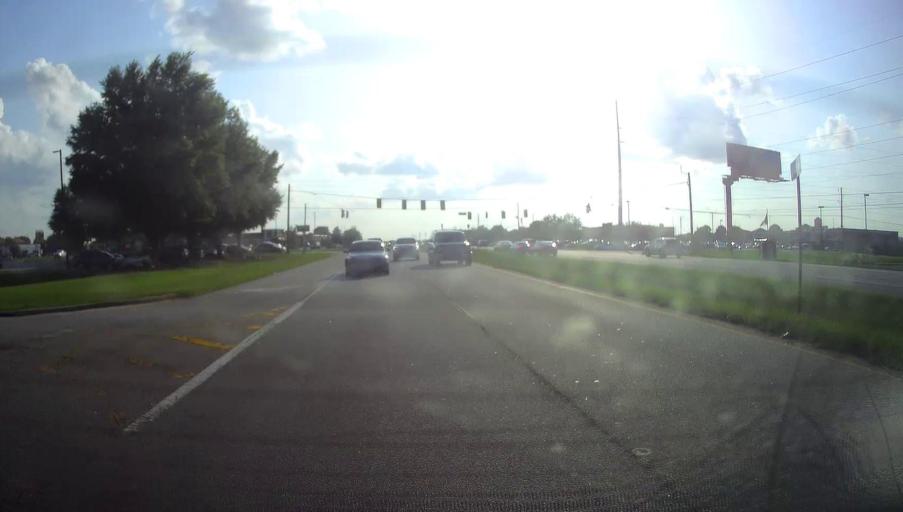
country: US
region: Georgia
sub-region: Houston County
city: Centerville
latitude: 32.6178
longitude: -83.6888
